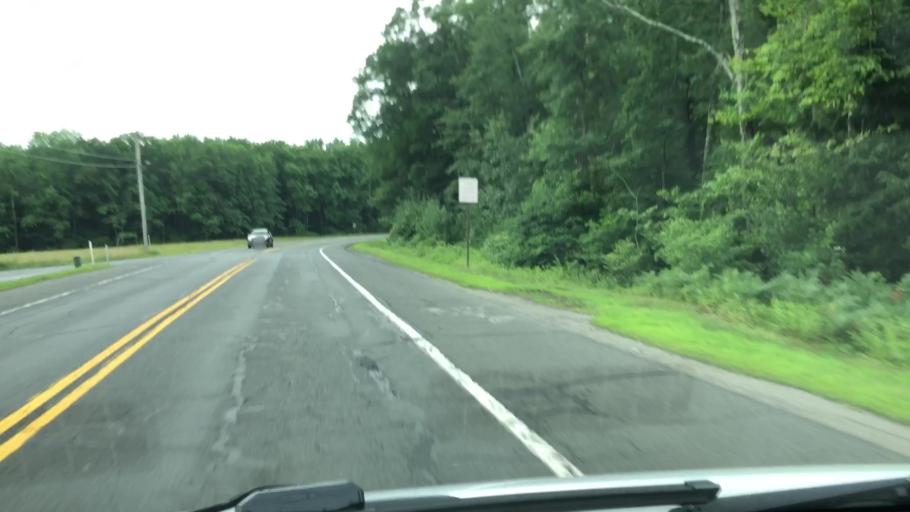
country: US
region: Massachusetts
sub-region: Franklin County
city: South Deerfield
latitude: 42.4632
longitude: -72.6188
